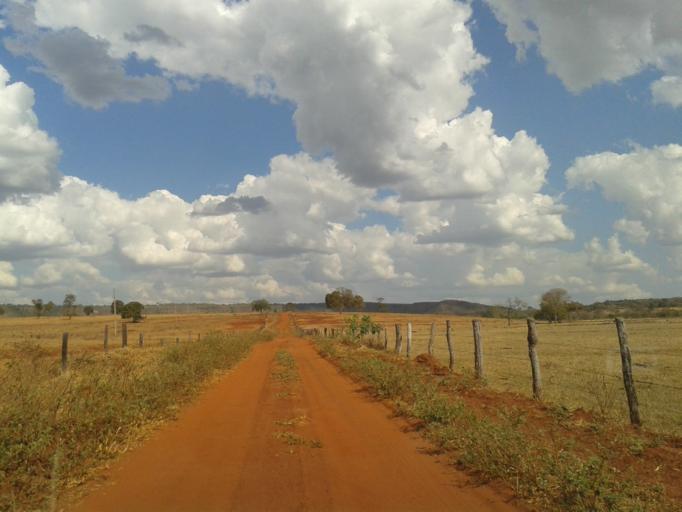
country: BR
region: Minas Gerais
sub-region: Santa Vitoria
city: Santa Vitoria
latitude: -19.2011
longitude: -49.9708
